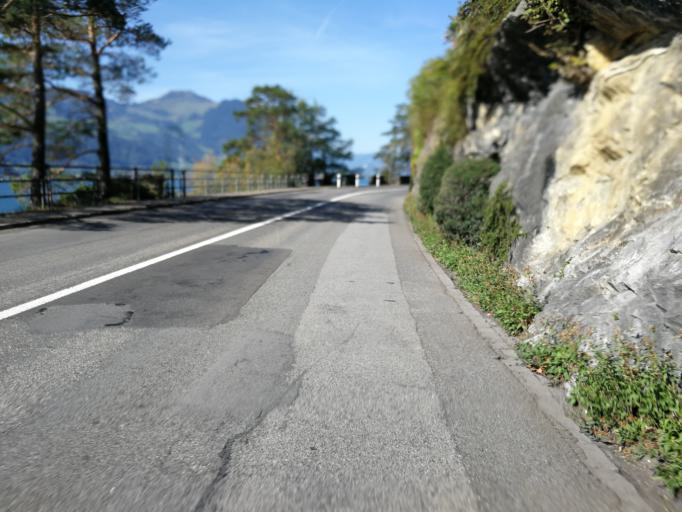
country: CH
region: Schwyz
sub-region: Bezirk Gersau
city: Gersau
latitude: 46.9882
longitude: 8.5386
